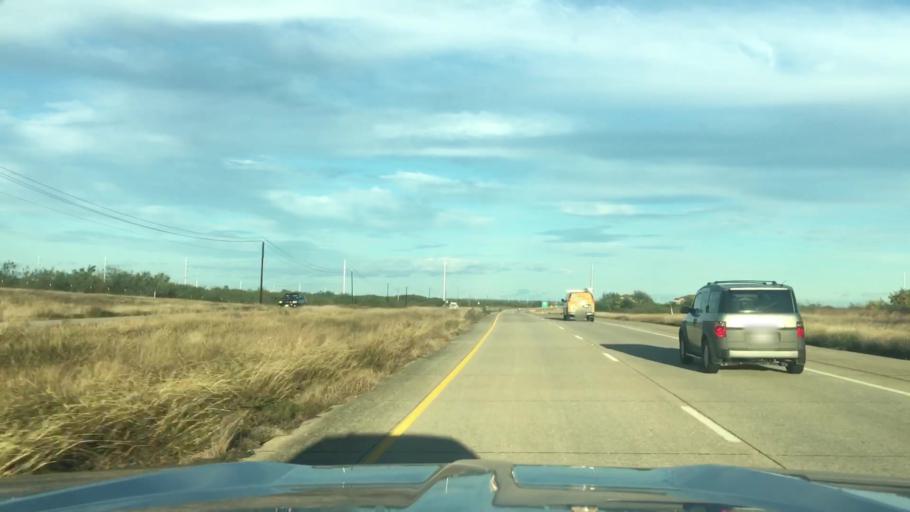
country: US
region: Texas
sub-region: Denton County
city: Denton
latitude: 33.2585
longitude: -97.1427
